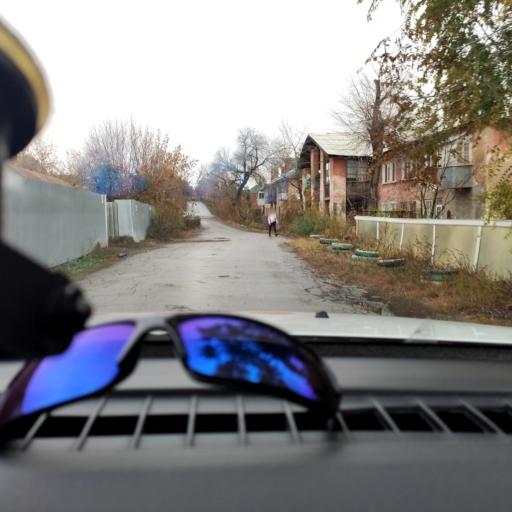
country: RU
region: Samara
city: Samara
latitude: 53.1725
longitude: 50.1733
